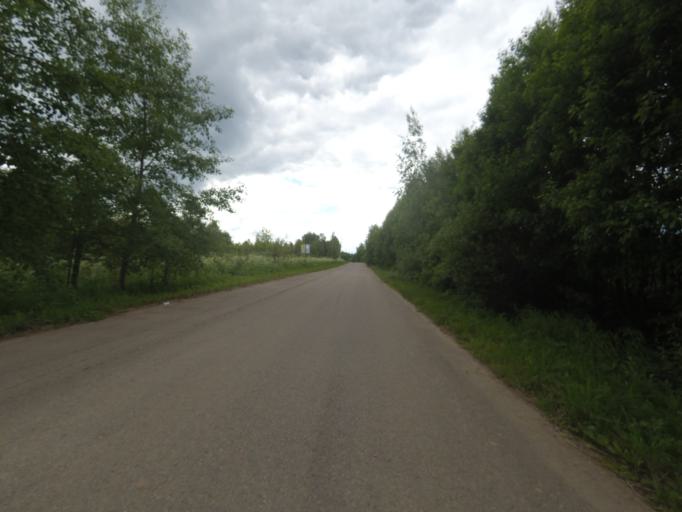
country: RU
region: Moskovskaya
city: Marfino
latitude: 56.0512
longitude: 37.6501
